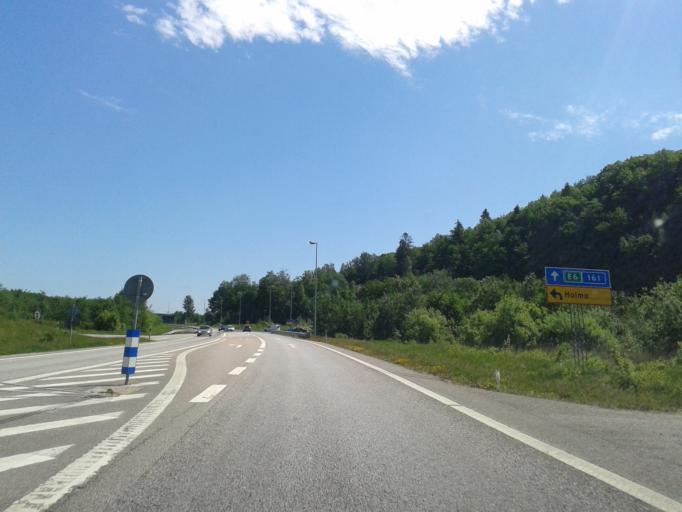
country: SE
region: Vaestra Goetaland
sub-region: Orust
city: Henan
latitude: 58.3455
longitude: 11.7561
